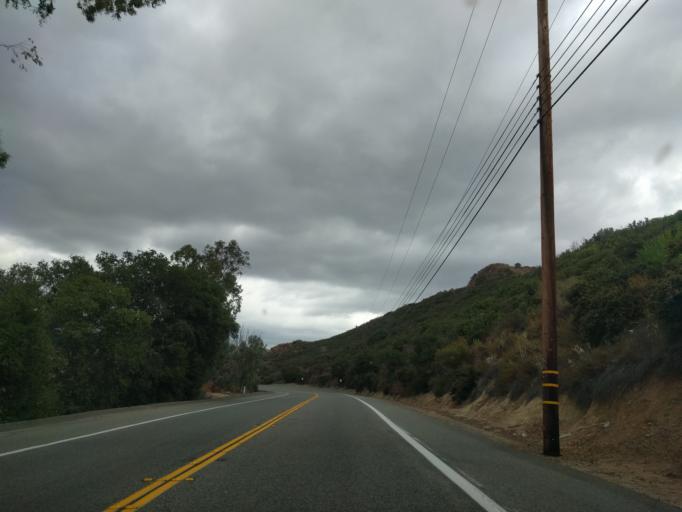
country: US
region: California
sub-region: Orange County
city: Foothill Ranch
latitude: 33.7487
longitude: -117.6791
